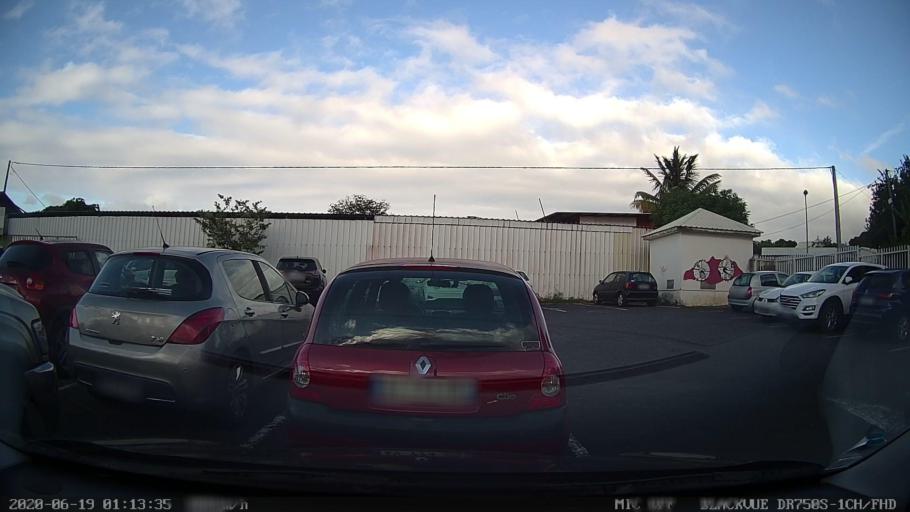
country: RE
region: Reunion
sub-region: Reunion
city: Sainte-Marie
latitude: -20.9026
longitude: 55.5078
